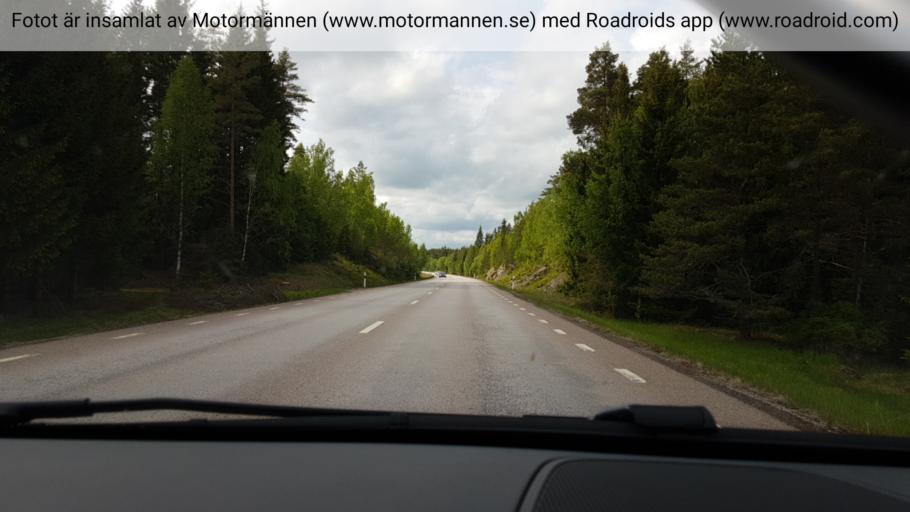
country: SE
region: Uppsala
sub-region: Tierps Kommun
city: Orbyhus
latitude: 60.2050
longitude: 17.7920
